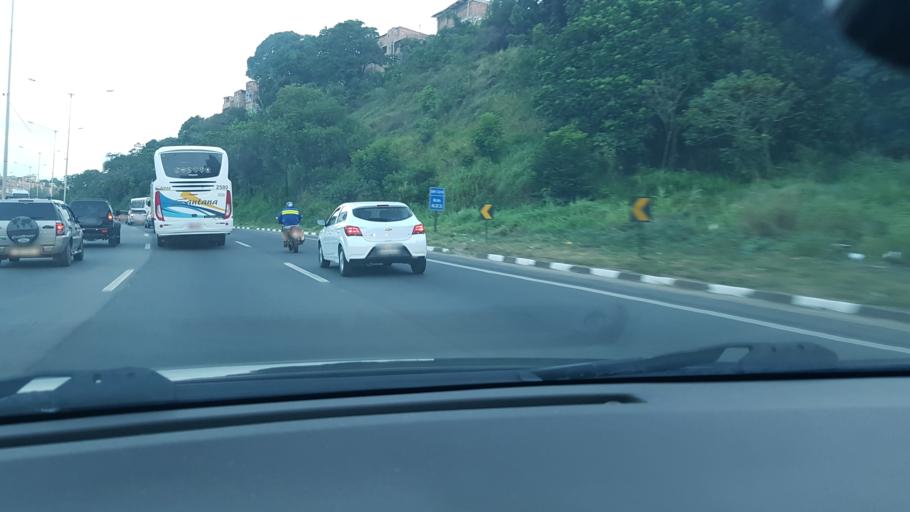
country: BR
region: Bahia
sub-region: Salvador
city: Salvador
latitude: -12.9368
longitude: -38.4725
